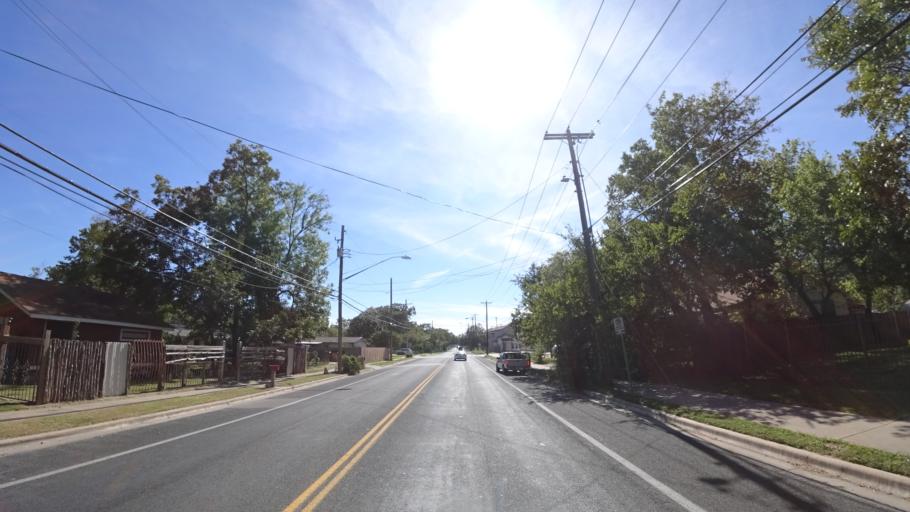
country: US
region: Texas
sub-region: Travis County
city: Austin
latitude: 30.2705
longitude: -97.6924
